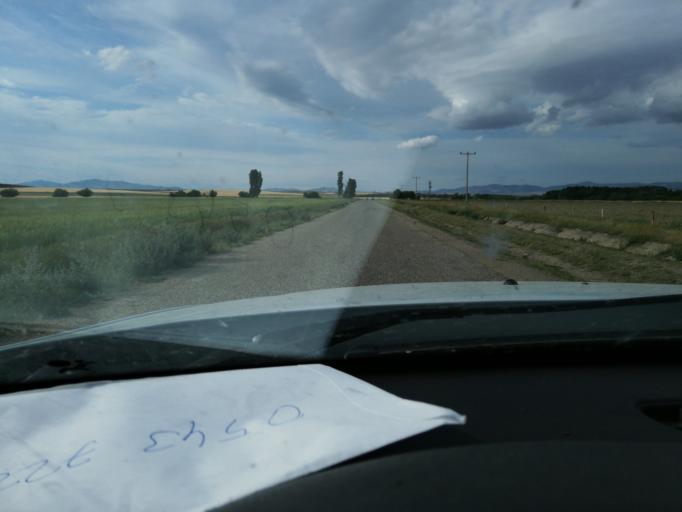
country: TR
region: Kirsehir
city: Kirsehir
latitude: 39.0053
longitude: 34.1197
